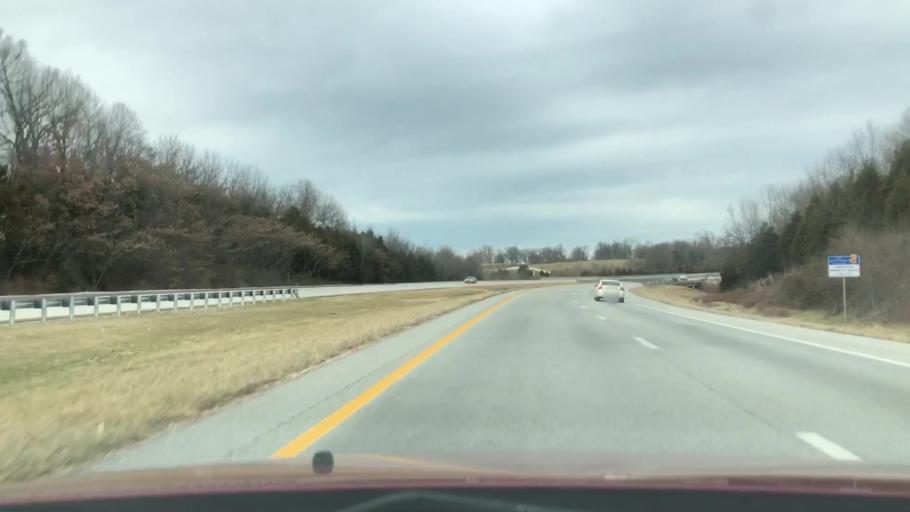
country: US
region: Missouri
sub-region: Greene County
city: Springfield
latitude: 37.2611
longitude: -93.2248
